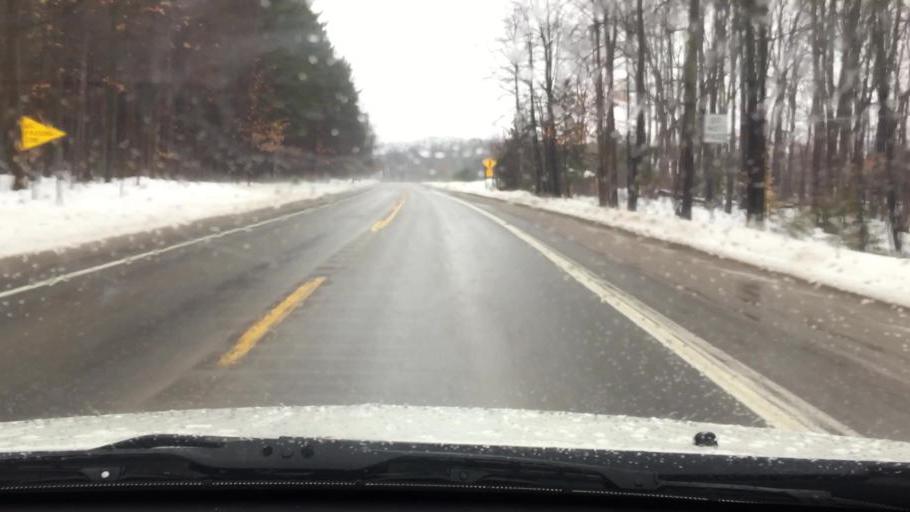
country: US
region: Michigan
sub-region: Charlevoix County
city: East Jordan
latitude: 45.2020
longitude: -85.1651
